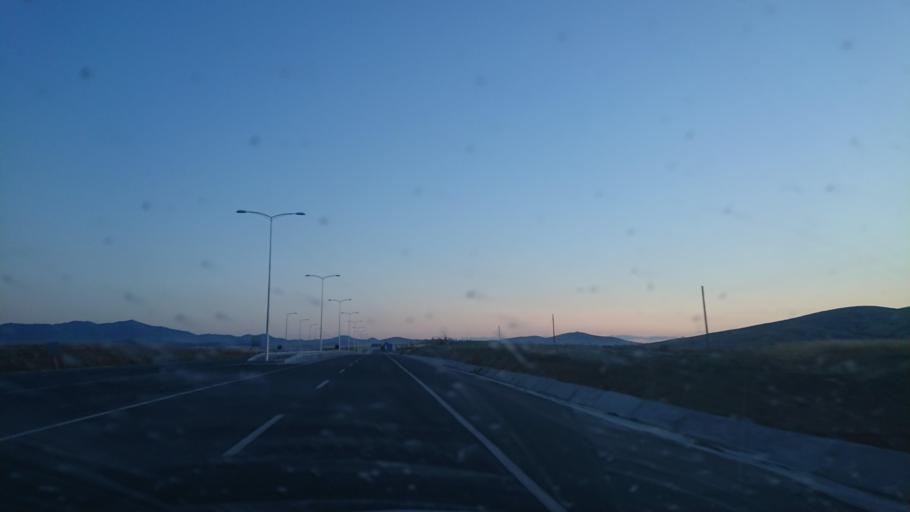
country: TR
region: Aksaray
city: Balci
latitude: 38.7782
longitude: 34.1131
